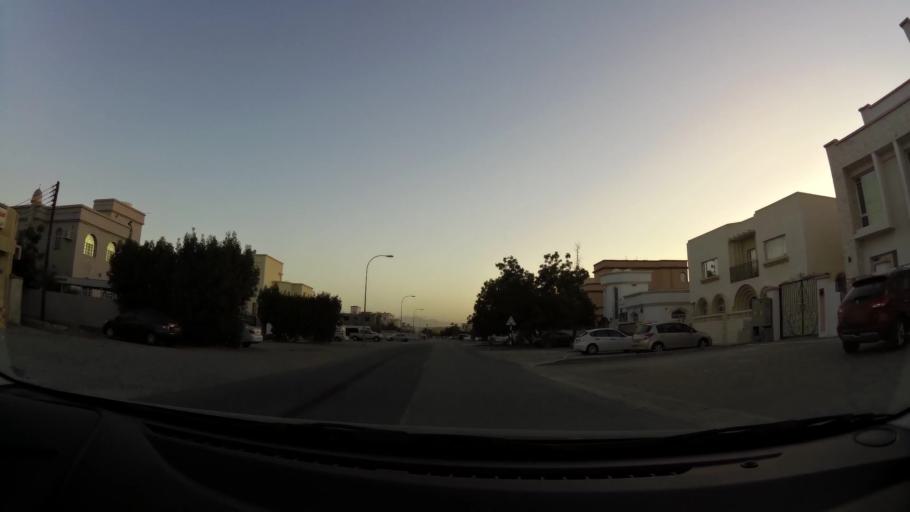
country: OM
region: Muhafazat Masqat
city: As Sib al Jadidah
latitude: 23.5953
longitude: 58.2310
